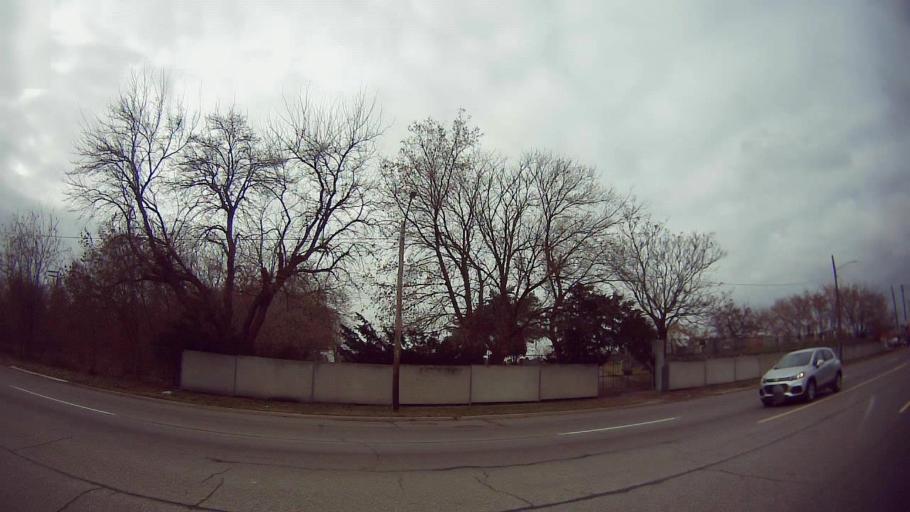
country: US
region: Michigan
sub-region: Wayne County
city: Hamtramck
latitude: 42.4000
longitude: -83.0229
